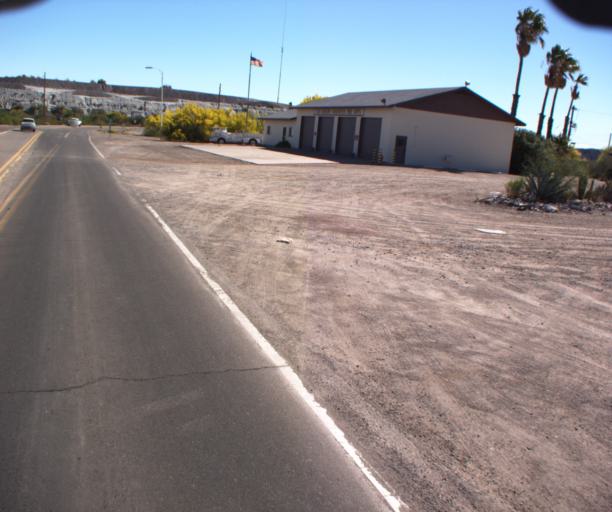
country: US
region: Arizona
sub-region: Pima County
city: Ajo
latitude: 32.3719
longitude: -112.8599
